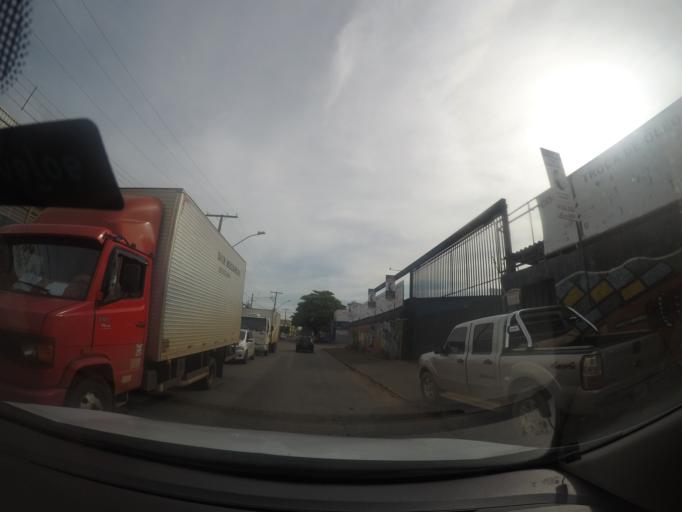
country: BR
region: Goias
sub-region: Goiania
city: Goiania
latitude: -16.6661
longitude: -49.3123
